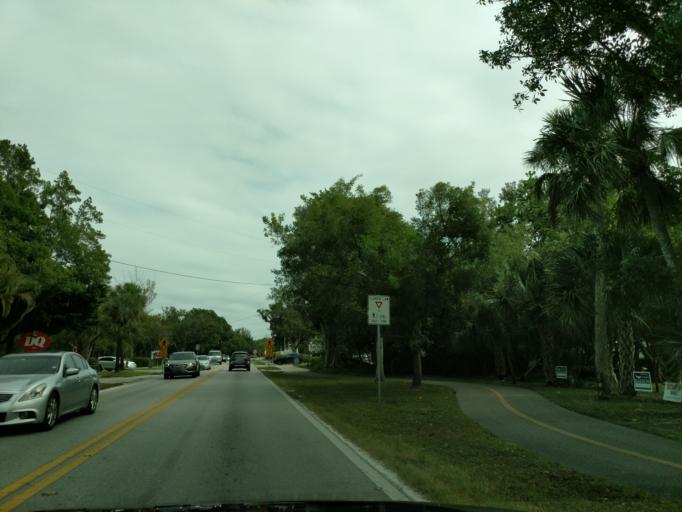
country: US
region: Florida
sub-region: Lee County
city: Sanibel
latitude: 26.4460
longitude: -82.0420
